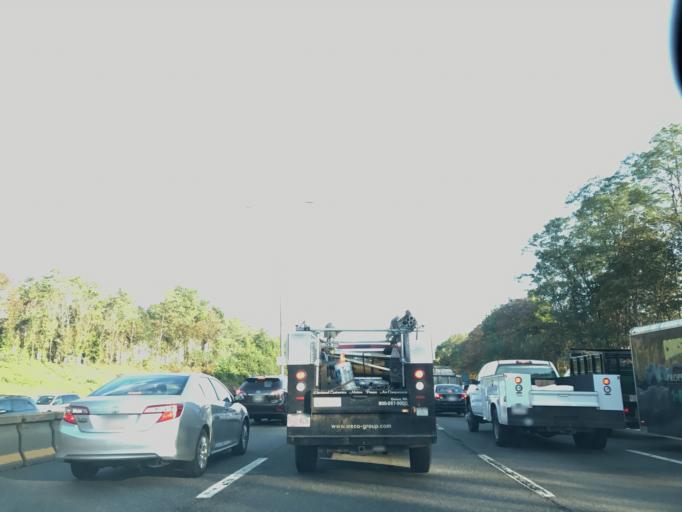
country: US
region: Massachusetts
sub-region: Norfolk County
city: Milton
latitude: 42.2487
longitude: -71.0373
